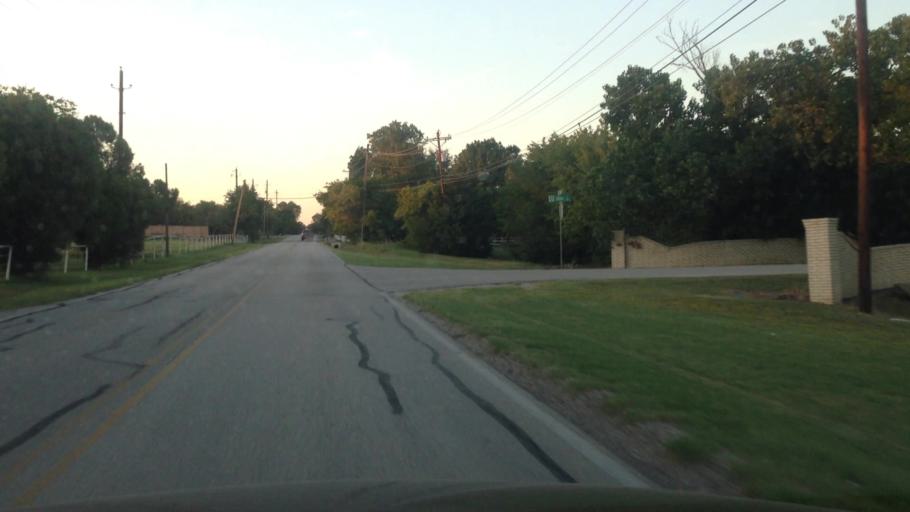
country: US
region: Texas
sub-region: Tarrant County
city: Keller
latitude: 32.9370
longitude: -97.2032
